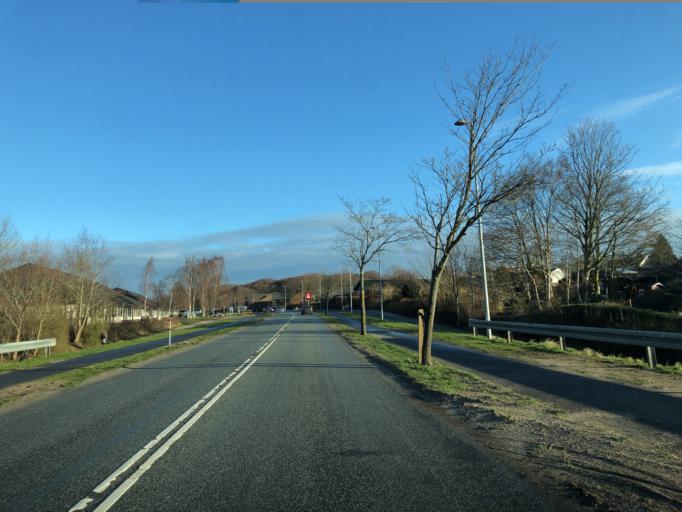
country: DK
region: Central Jutland
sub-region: Favrskov Kommune
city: Hinnerup
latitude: 56.2579
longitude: 10.0707
